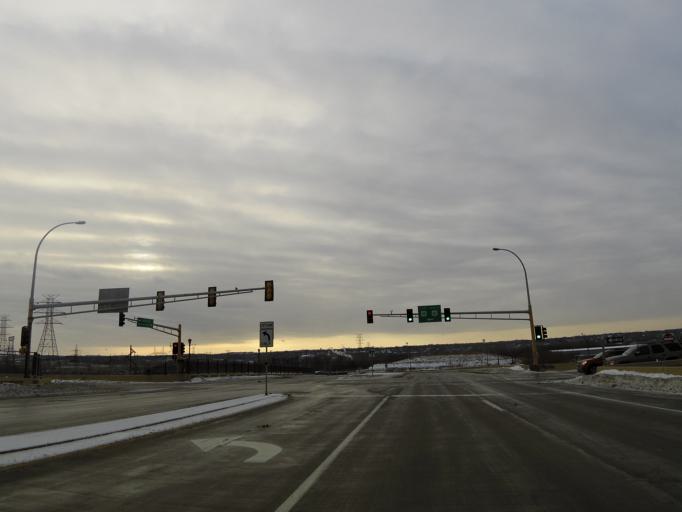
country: US
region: Minnesota
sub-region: Washington County
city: Newport
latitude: 44.8914
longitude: -93.0067
